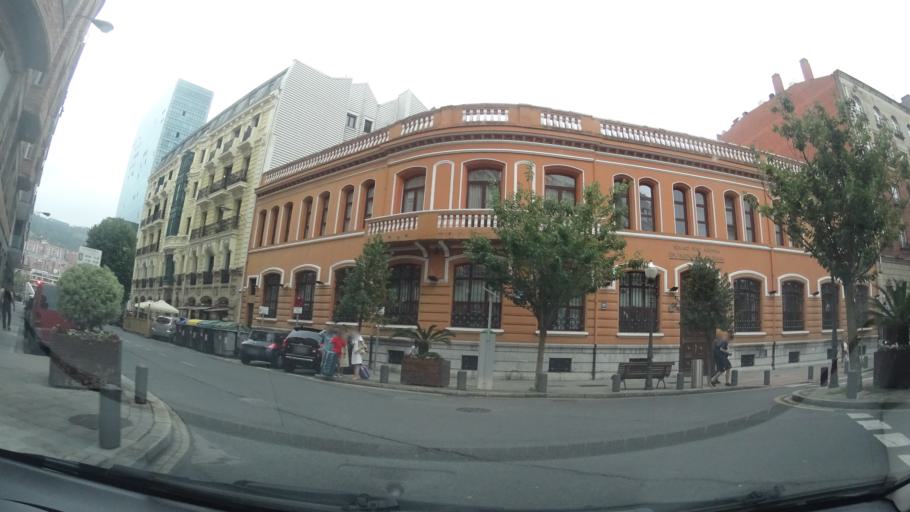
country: ES
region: Basque Country
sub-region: Bizkaia
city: Bilbao
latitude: 43.2652
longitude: -2.9306
